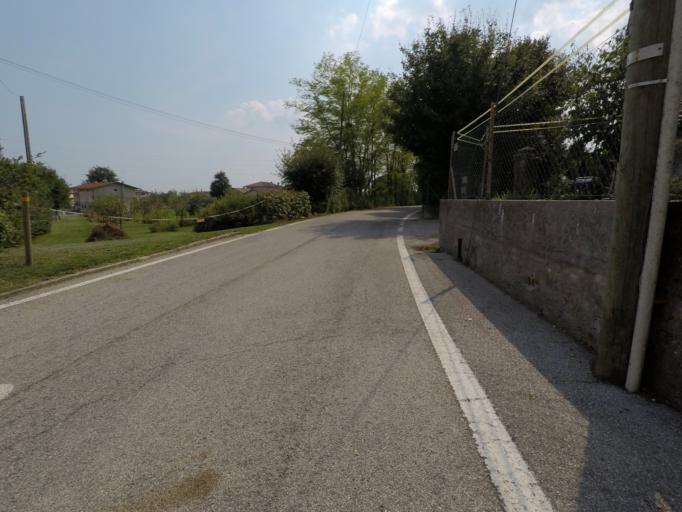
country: IT
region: Friuli Venezia Giulia
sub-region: Provincia di Pordenone
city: Caneva
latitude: 45.9679
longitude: 12.4452
